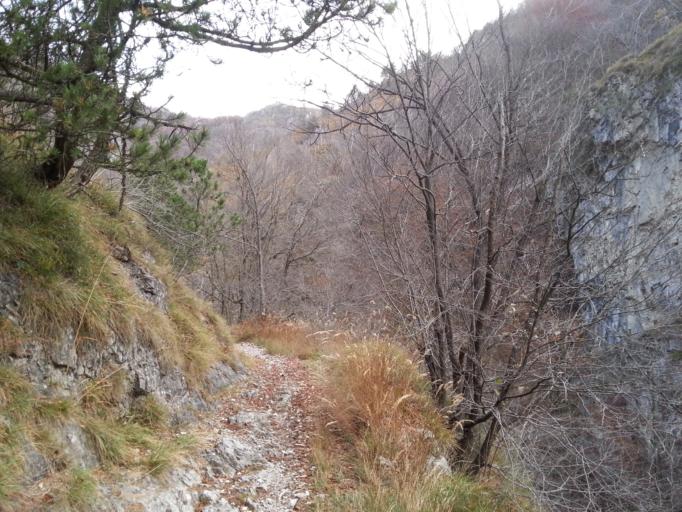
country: IT
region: Lombardy
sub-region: Provincia di Lecco
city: Morterone
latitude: 45.8859
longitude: 9.4619
